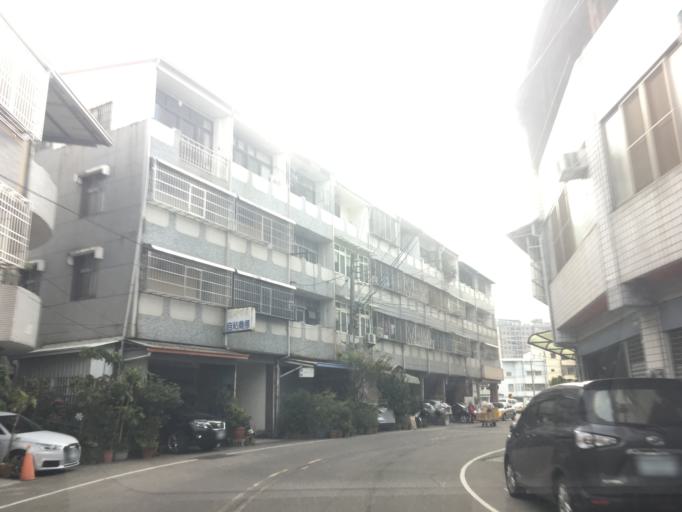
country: TW
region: Taiwan
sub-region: Taichung City
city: Taichung
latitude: 24.1923
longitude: 120.6983
